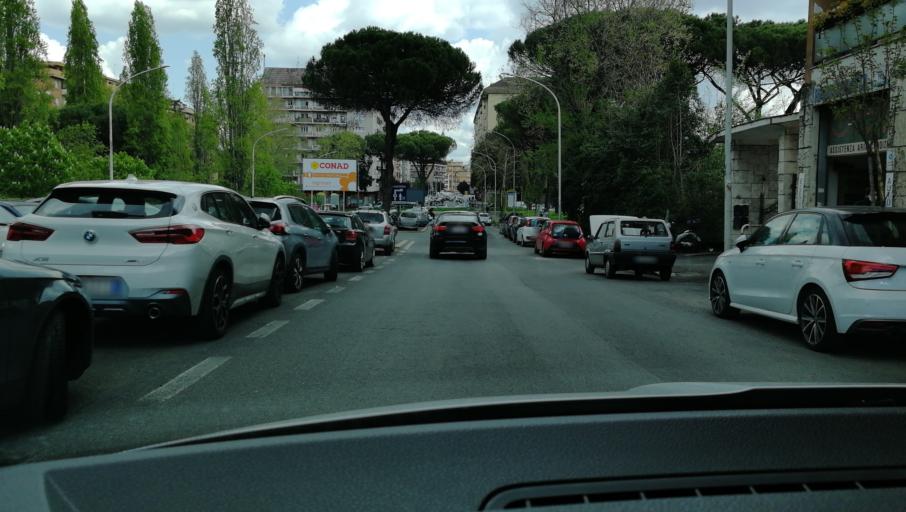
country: IT
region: Latium
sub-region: Citta metropolitana di Roma Capitale
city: Rome
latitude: 41.8501
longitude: 12.4916
